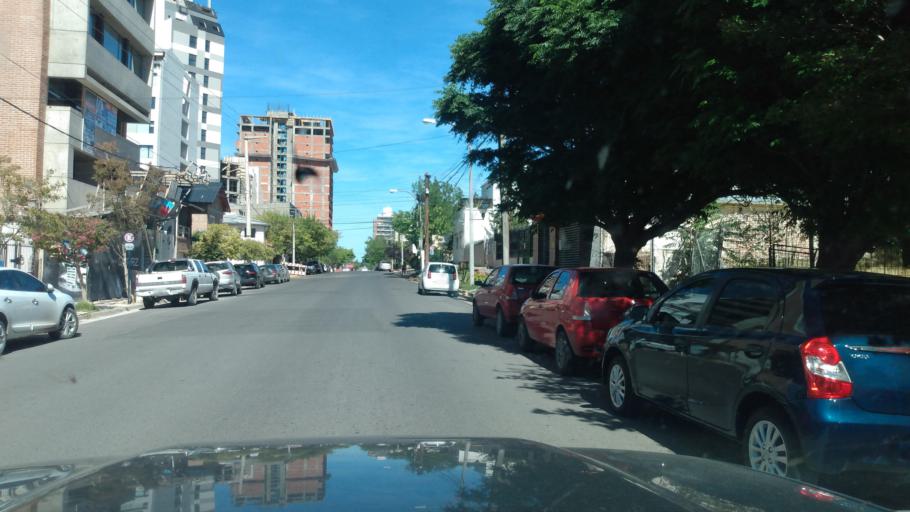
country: AR
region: Neuquen
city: Neuquen
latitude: -38.9475
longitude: -68.0612
